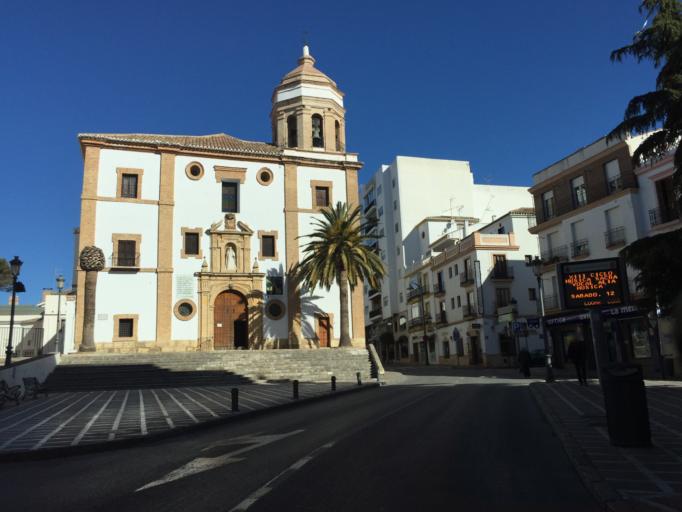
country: ES
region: Andalusia
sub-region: Provincia de Malaga
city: Ronda
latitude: 36.7440
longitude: -5.1672
